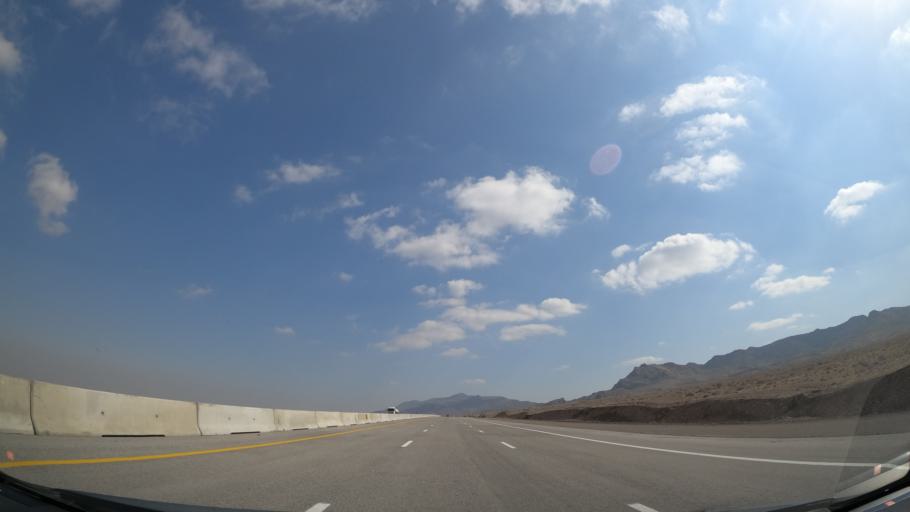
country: IR
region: Alborz
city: Eshtehard
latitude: 35.7091
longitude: 50.6004
